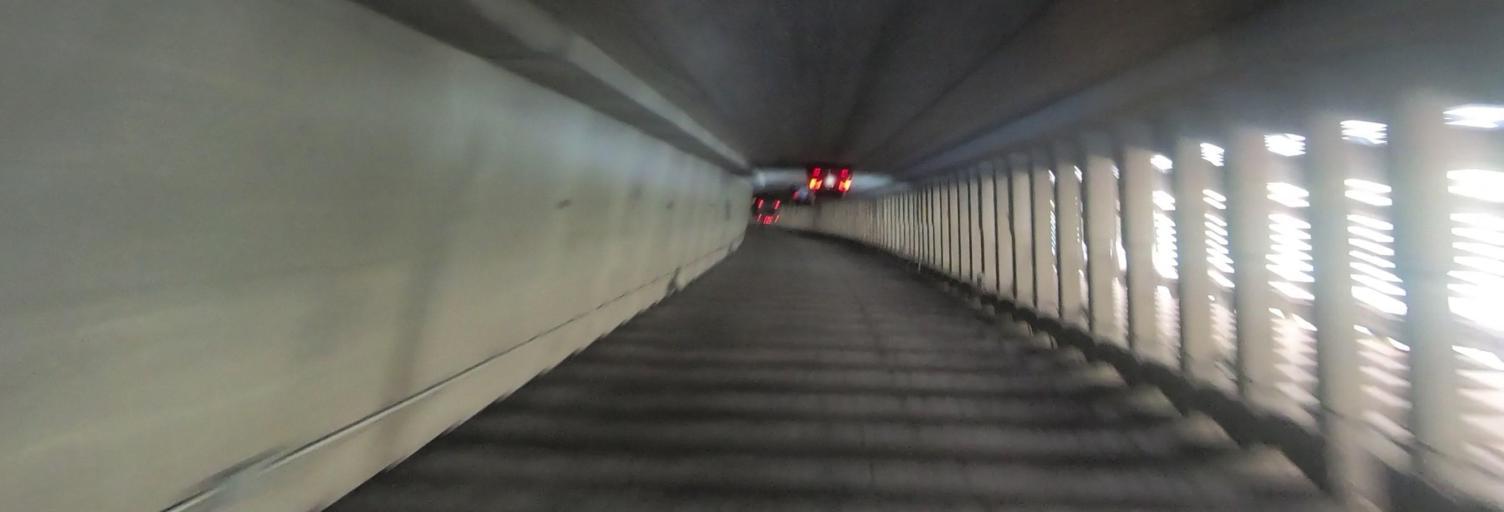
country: CA
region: British Columbia
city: Golden
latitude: 51.3291
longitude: -117.4611
